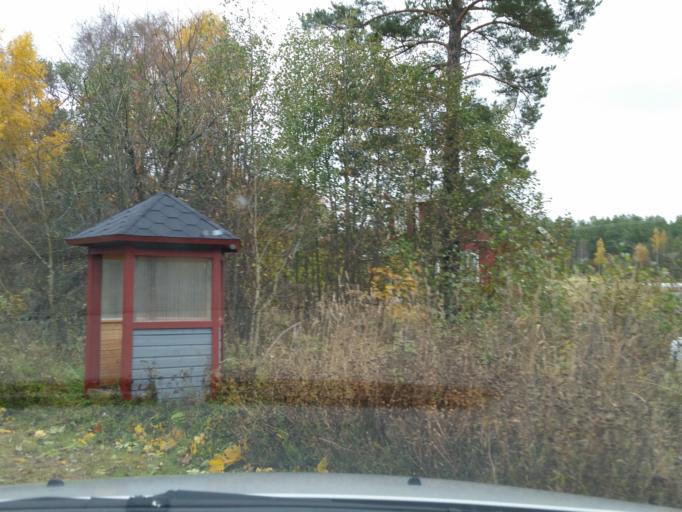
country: AX
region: Alands landsbygd
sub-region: Lumparland
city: Lumparland
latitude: 60.1338
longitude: 20.2407
